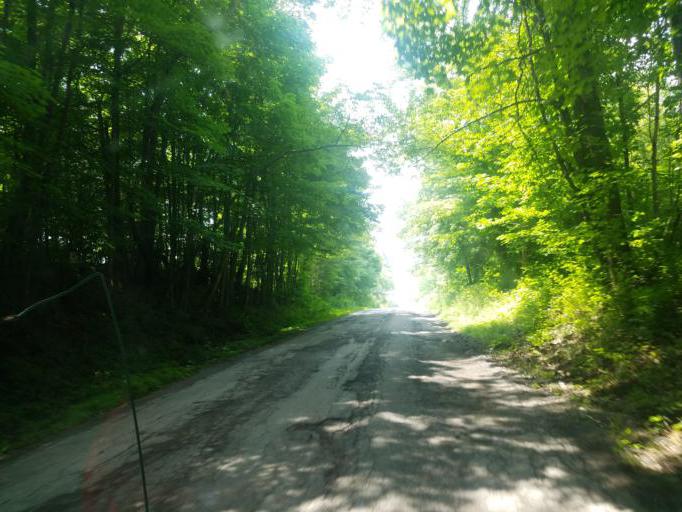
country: US
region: Ohio
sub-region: Columbiana County
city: Salem
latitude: 40.9730
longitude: -80.8239
